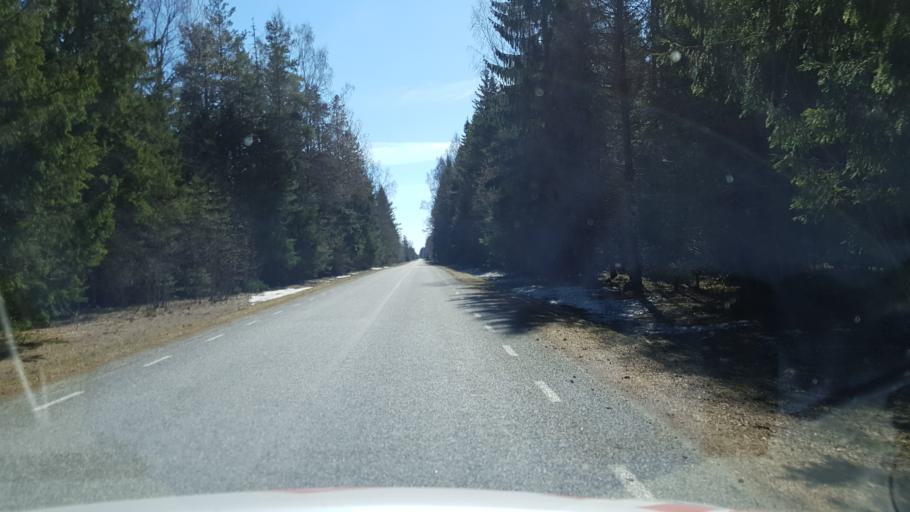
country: EE
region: Laeaene-Virumaa
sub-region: Vinni vald
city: Vinni
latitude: 59.1704
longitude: 26.5075
